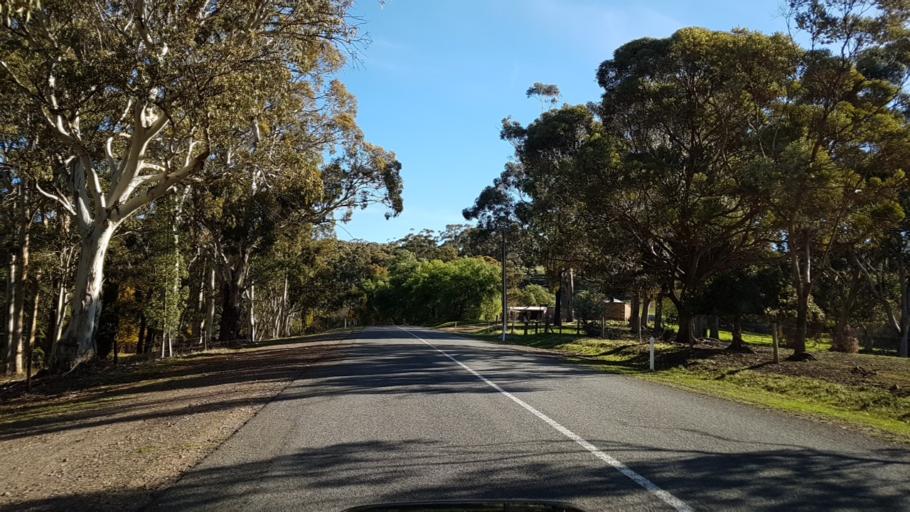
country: AU
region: South Australia
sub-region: Northern Areas
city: Jamestown
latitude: -33.2773
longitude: 138.5708
